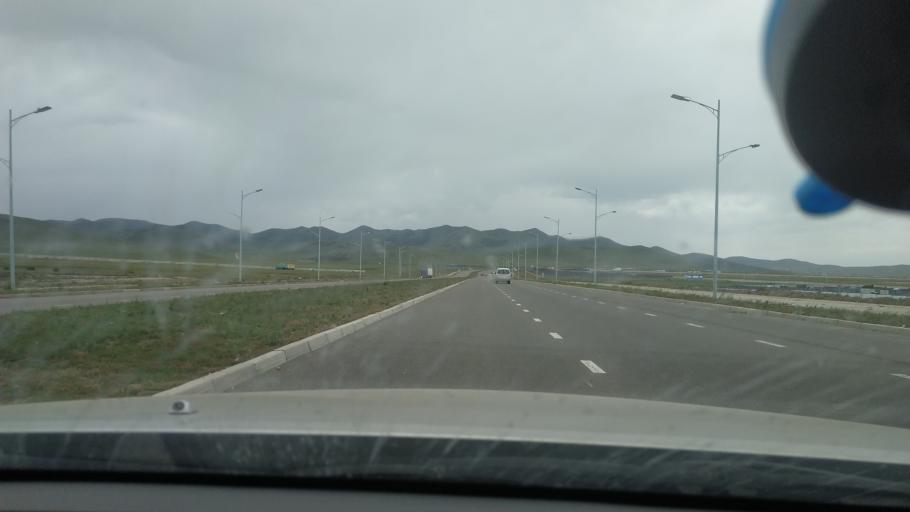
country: MN
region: Ulaanbaatar
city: Ulaanbaatar
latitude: 47.8367
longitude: 106.7887
